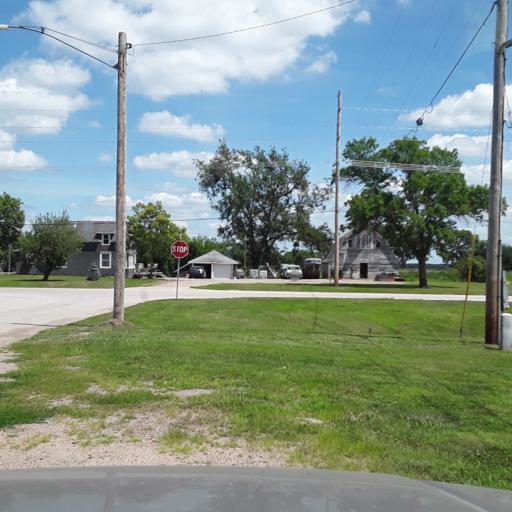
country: US
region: Nebraska
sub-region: Nance County
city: Genoa
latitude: 41.4426
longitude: -97.7352
